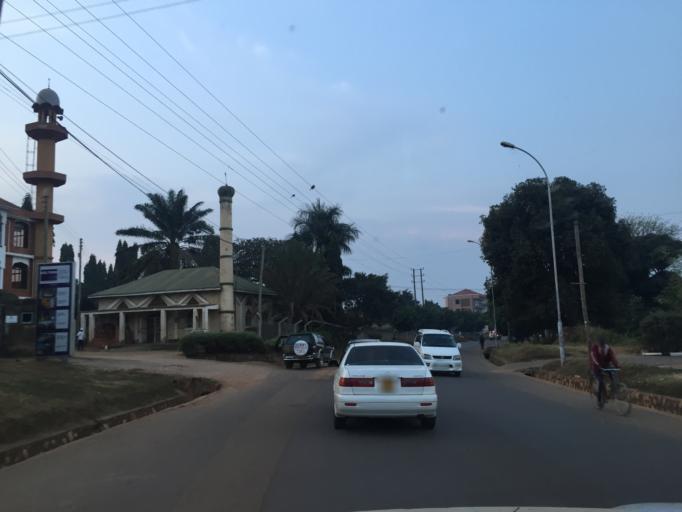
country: UG
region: Central Region
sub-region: Kampala District
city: Kampala
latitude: 0.2497
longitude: 32.6258
